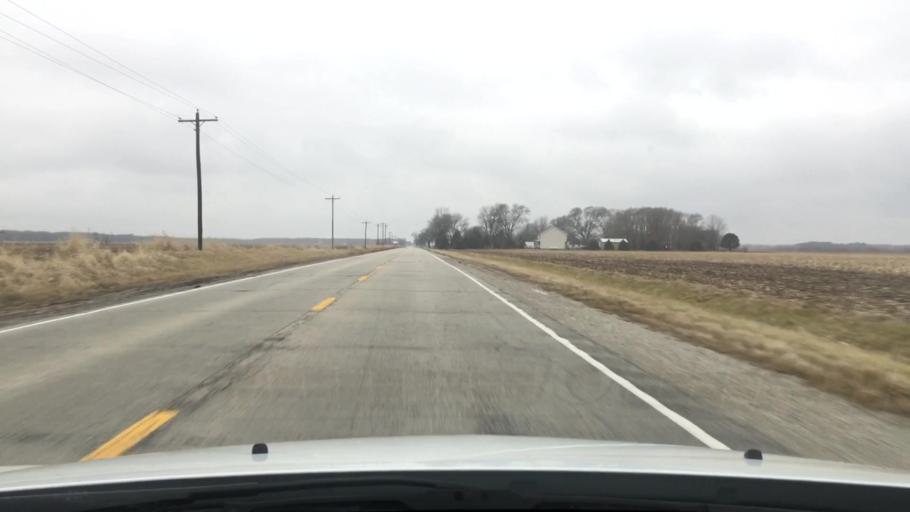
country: US
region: Illinois
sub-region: Iroquois County
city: Watseka
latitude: 40.8888
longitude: -87.7899
